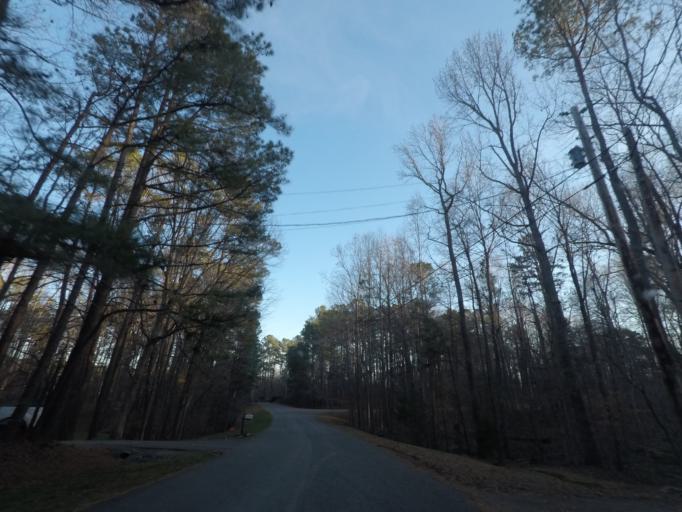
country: US
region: North Carolina
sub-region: Durham County
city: Durham
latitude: 36.0834
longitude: -78.9708
